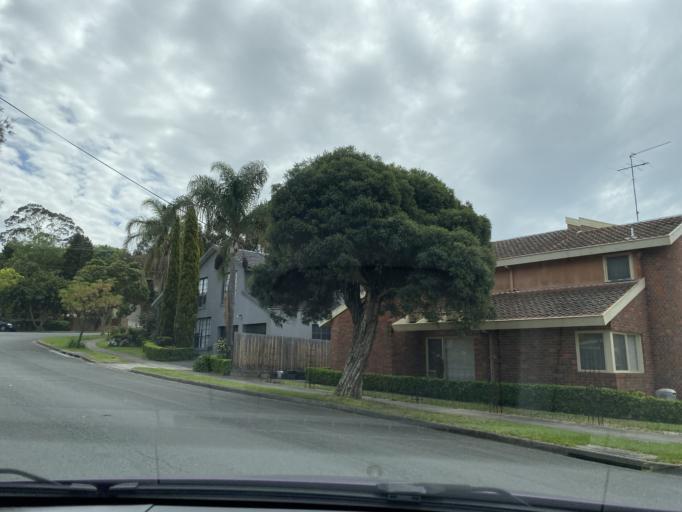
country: AU
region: Victoria
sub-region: Manningham
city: Templestowe Lower
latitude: -37.7687
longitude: 145.1260
